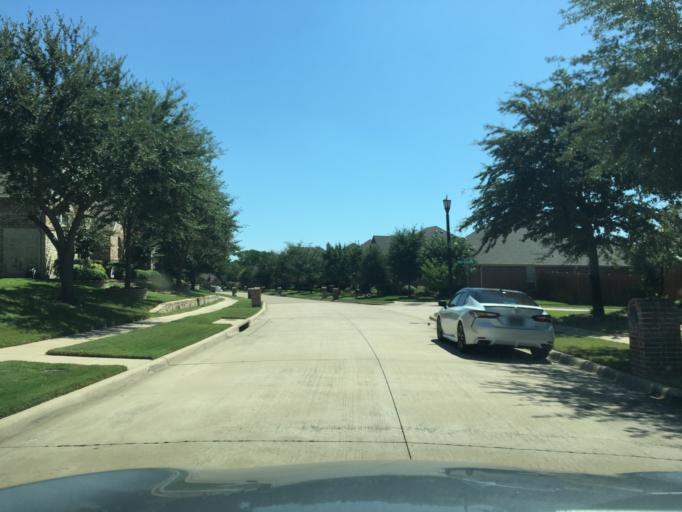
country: US
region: Texas
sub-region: Dallas County
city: Sachse
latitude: 32.9663
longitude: -96.6155
